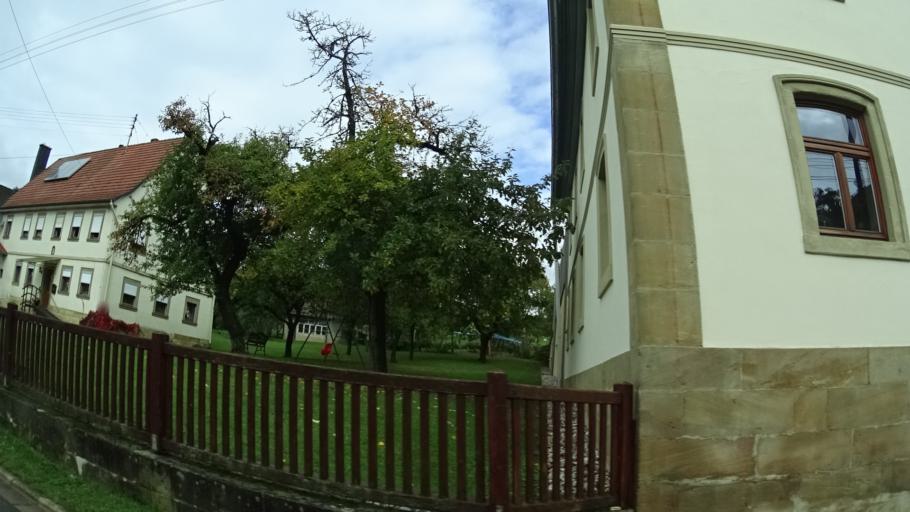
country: DE
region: Bavaria
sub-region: Upper Franconia
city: Schesslitz
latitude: 50.0126
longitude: 10.9904
